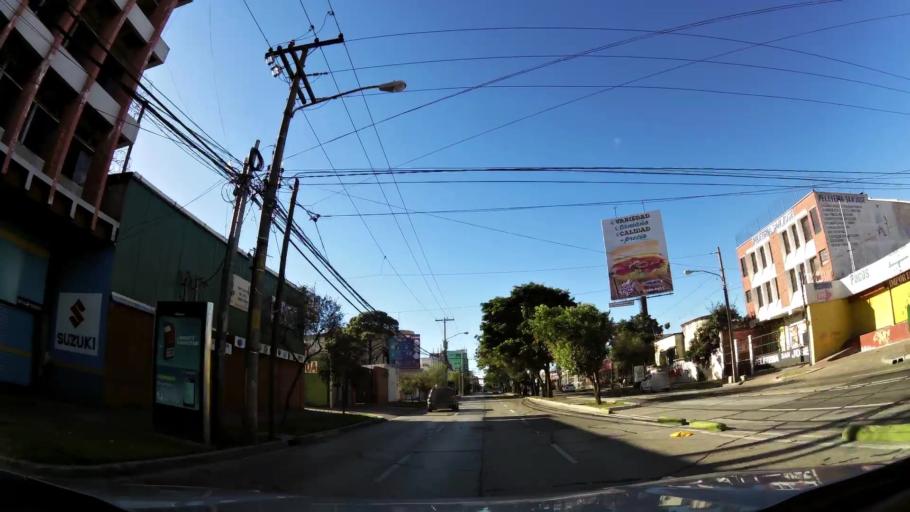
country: GT
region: Guatemala
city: Guatemala City
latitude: 14.6162
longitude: -90.5177
